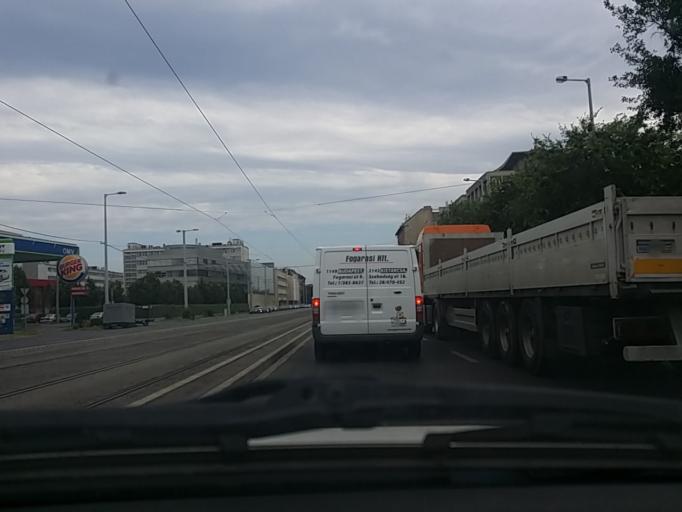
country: HU
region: Budapest
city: Budapest XIV. keruelet
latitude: 47.5084
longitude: 19.1026
